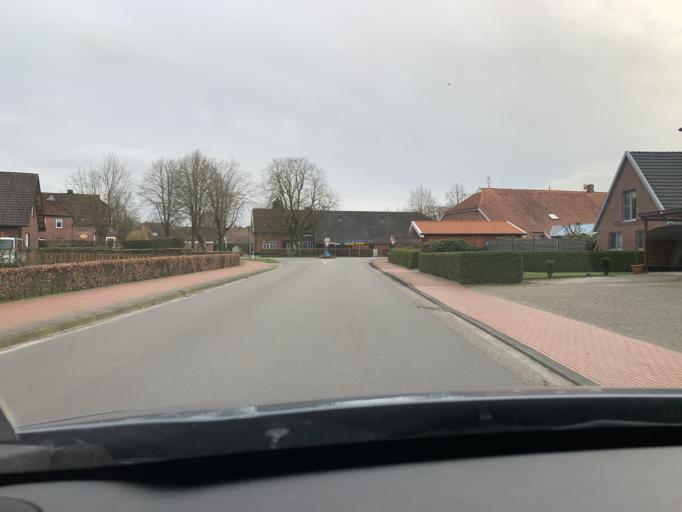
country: DE
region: Lower Saxony
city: Detern
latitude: 53.2552
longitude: 7.7105
